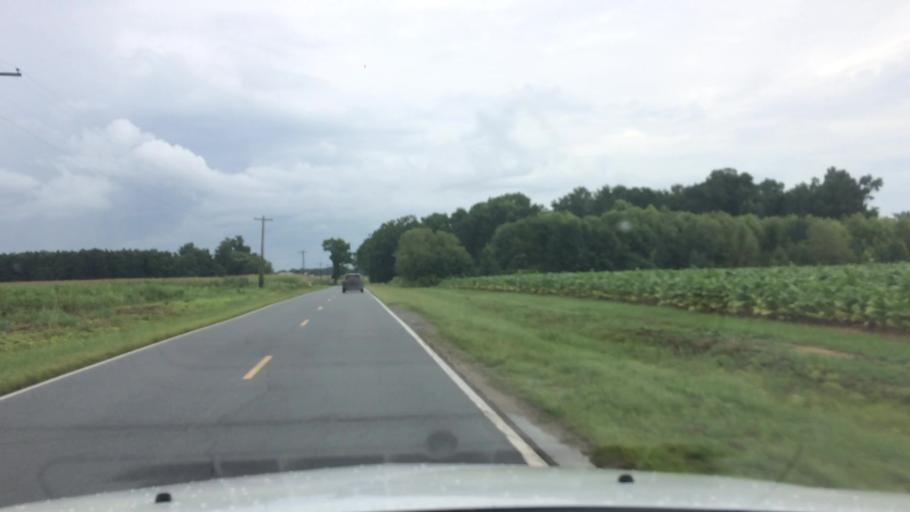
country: US
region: North Carolina
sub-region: Pitt County
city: Farmville
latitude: 35.5679
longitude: -77.5484
